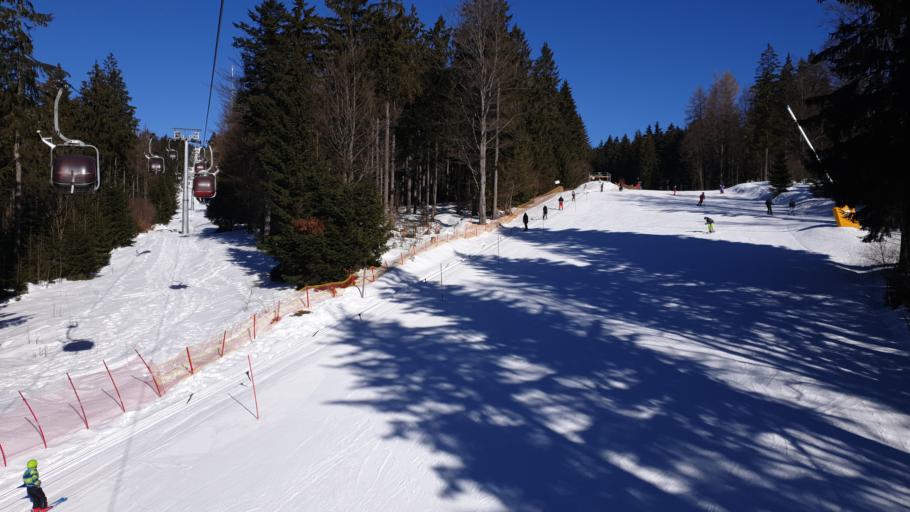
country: DE
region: Bavaria
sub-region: Upper Franconia
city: Warmensteinach
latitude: 50.0146
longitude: 11.8087
